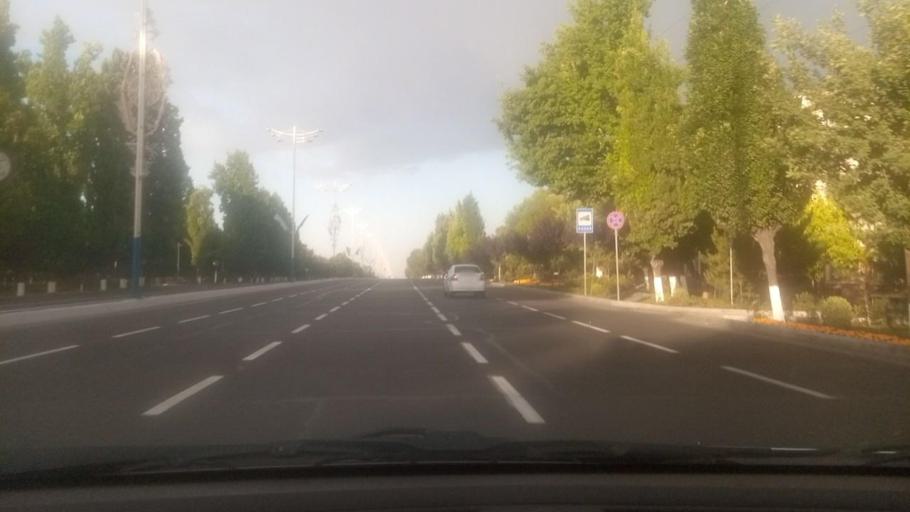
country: UZ
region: Toshkent
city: Salor
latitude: 41.3344
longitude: 69.3348
